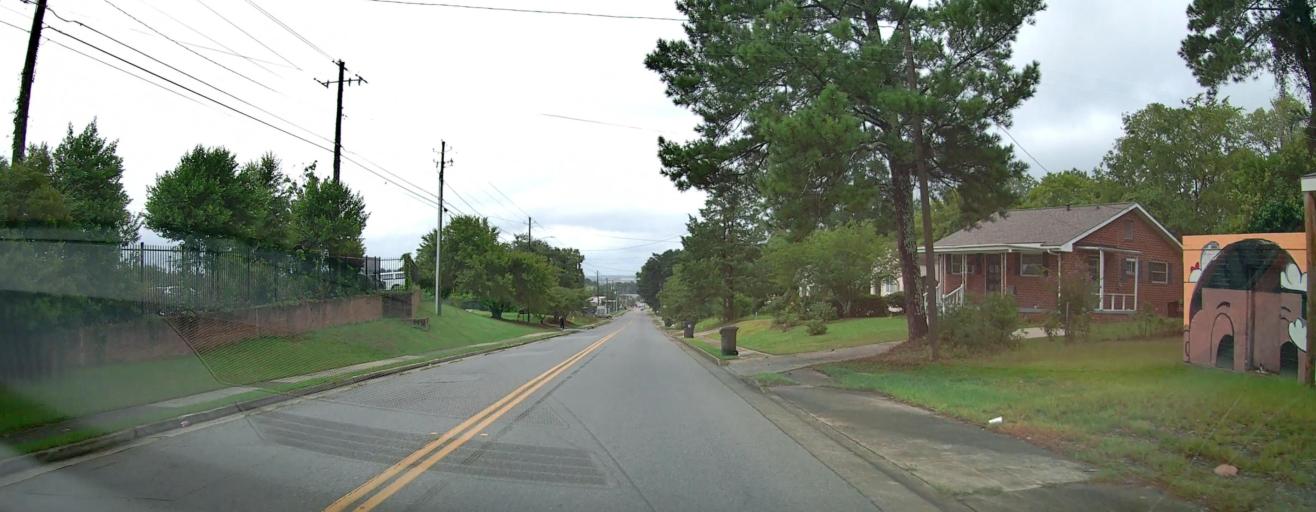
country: US
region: Georgia
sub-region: Bibb County
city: Macon
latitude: 32.8579
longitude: -83.6185
